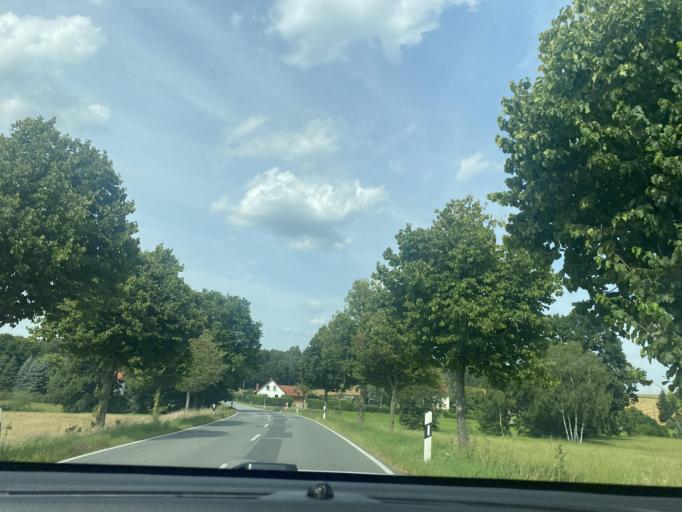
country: DE
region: Saxony
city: Grosshennersdorf
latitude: 51.0027
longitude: 14.7954
